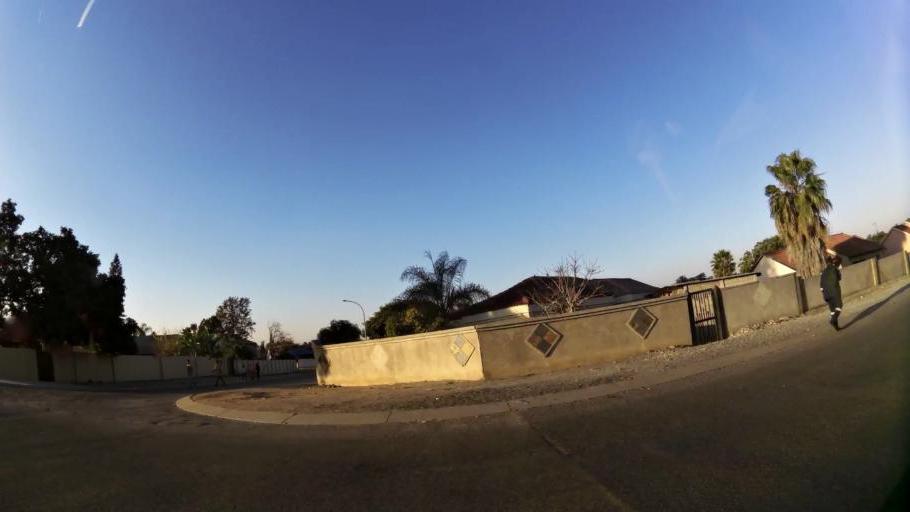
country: ZA
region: North-West
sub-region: Bojanala Platinum District Municipality
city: Rustenburg
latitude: -25.6387
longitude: 27.2031
